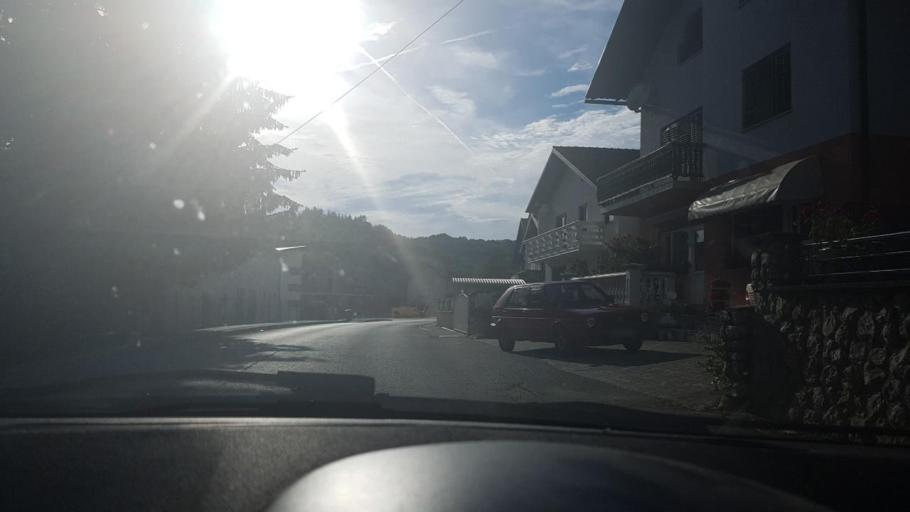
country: HR
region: Varazdinska
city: Lepoglava
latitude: 46.2293
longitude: 15.9792
